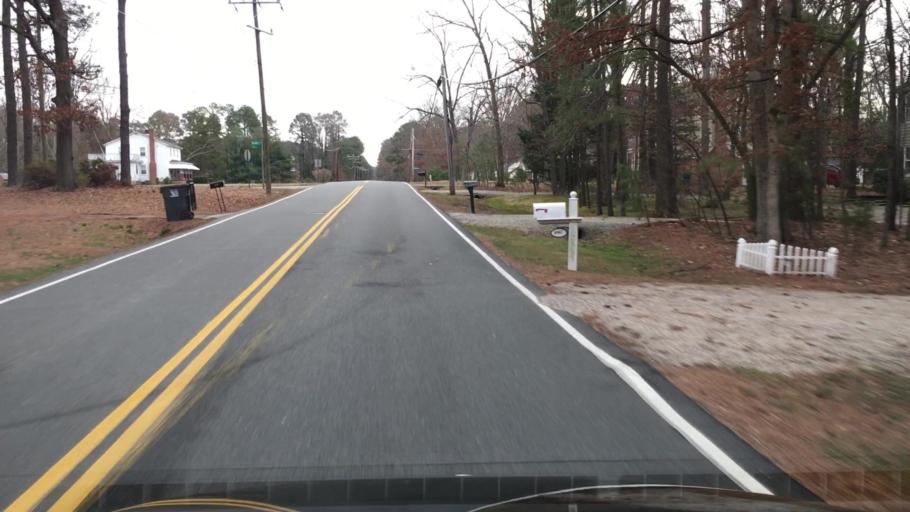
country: US
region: Virginia
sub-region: Henrico County
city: Tuckahoe
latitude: 37.5883
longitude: -77.5817
